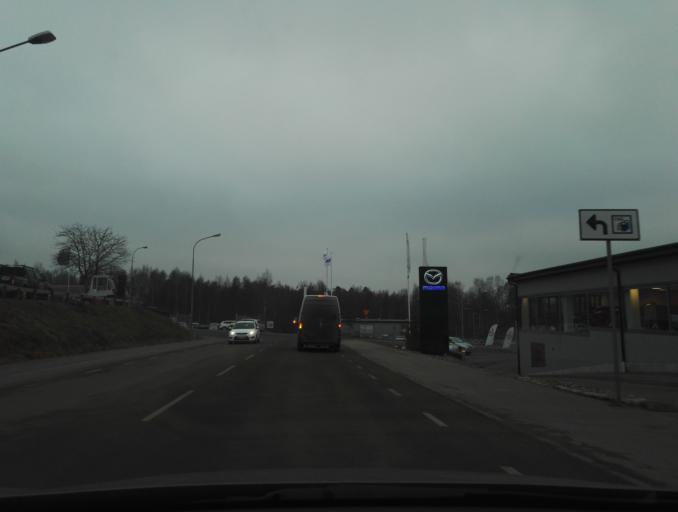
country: SE
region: Kronoberg
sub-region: Vaxjo Kommun
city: Vaexjoe
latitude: 56.8882
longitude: 14.7601
